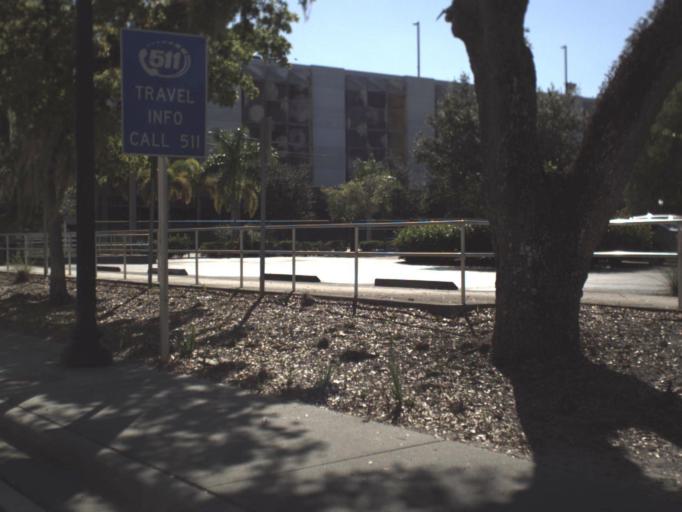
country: US
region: Florida
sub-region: Lee County
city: North Fort Myers
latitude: 26.6408
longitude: -81.8709
